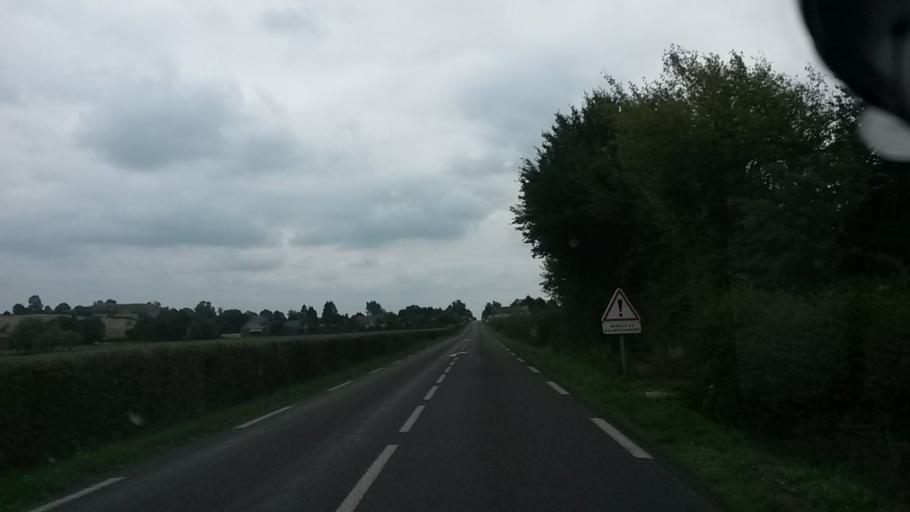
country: FR
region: Haute-Normandie
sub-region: Departement de la Seine-Maritime
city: Forges-les-Eaux
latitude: 49.5751
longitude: 1.5402
